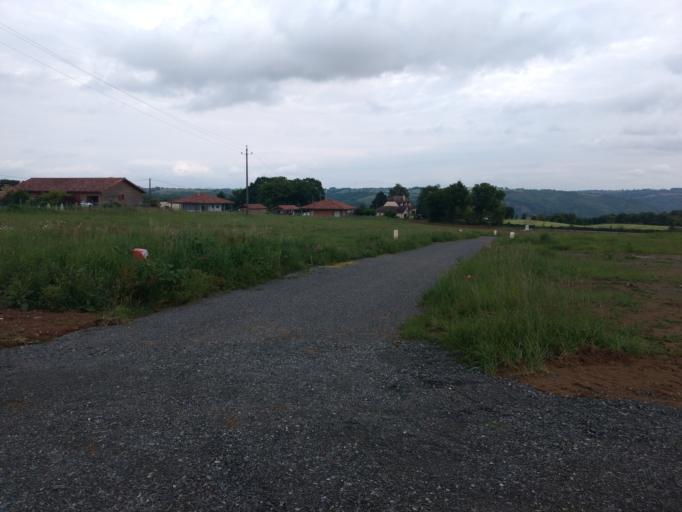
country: FR
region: Midi-Pyrenees
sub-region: Departement de l'Aveyron
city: Capdenac-Gare
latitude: 44.5398
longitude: 2.1116
